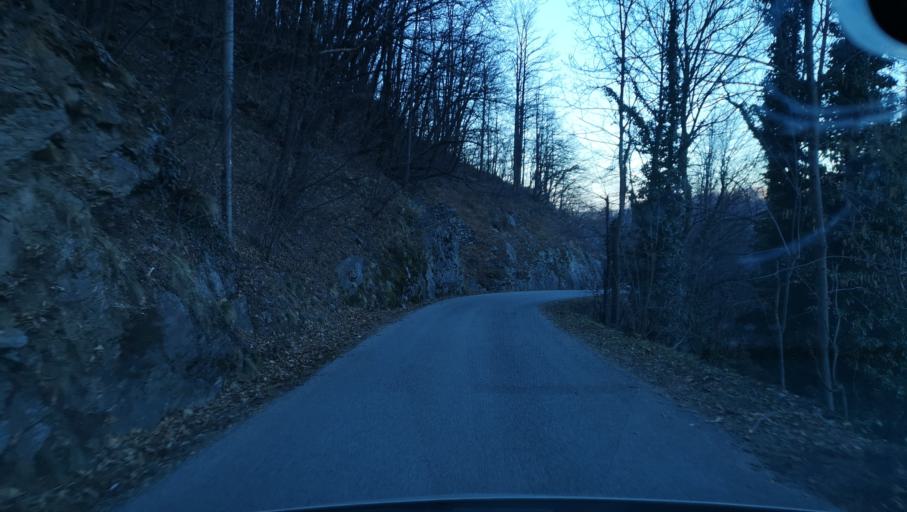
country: IT
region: Piedmont
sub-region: Provincia di Torino
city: Rora
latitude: 44.7879
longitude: 7.1911
